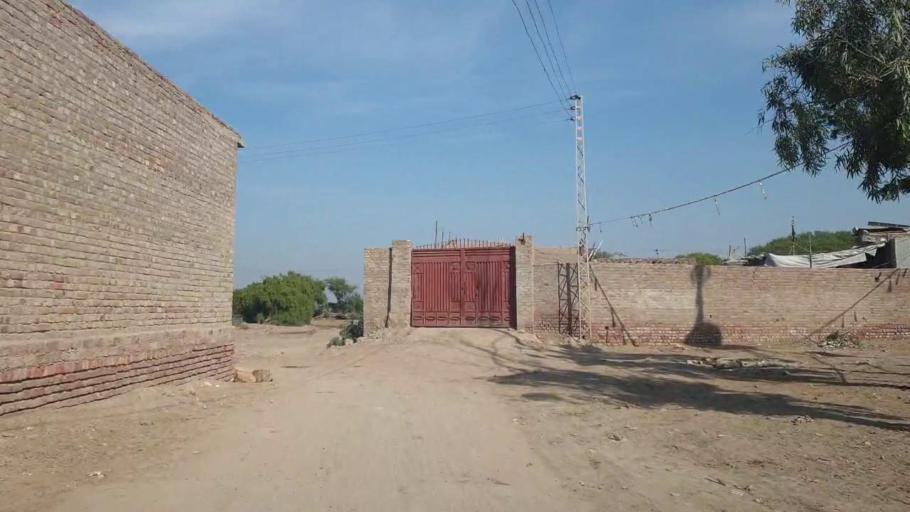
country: PK
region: Sindh
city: Matiari
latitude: 25.6439
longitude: 68.3544
